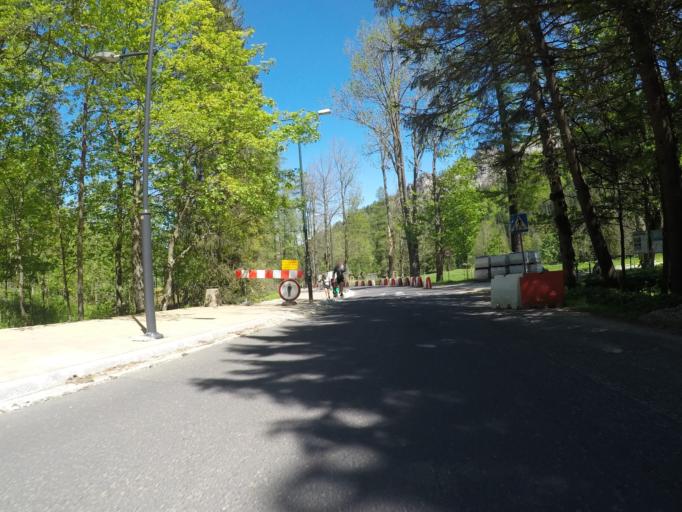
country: PL
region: Lesser Poland Voivodeship
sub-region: Powiat tatrzanski
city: Zakopane
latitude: 49.2724
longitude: 19.9809
